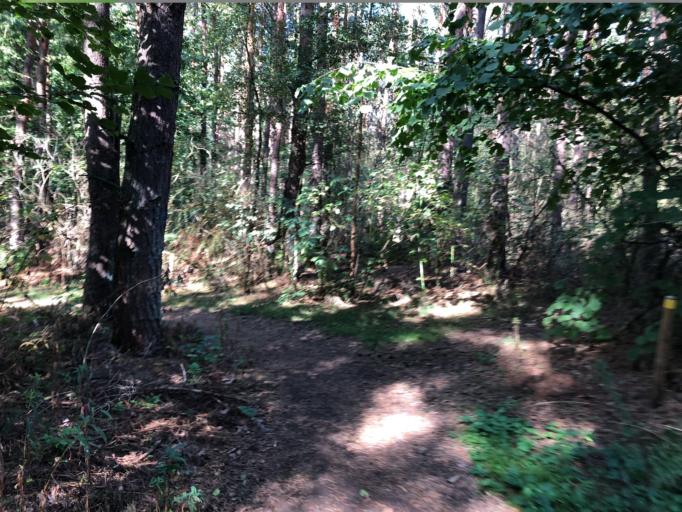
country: SE
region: Skane
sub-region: Lomma Kommun
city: Lomma
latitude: 55.6914
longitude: 13.0649
